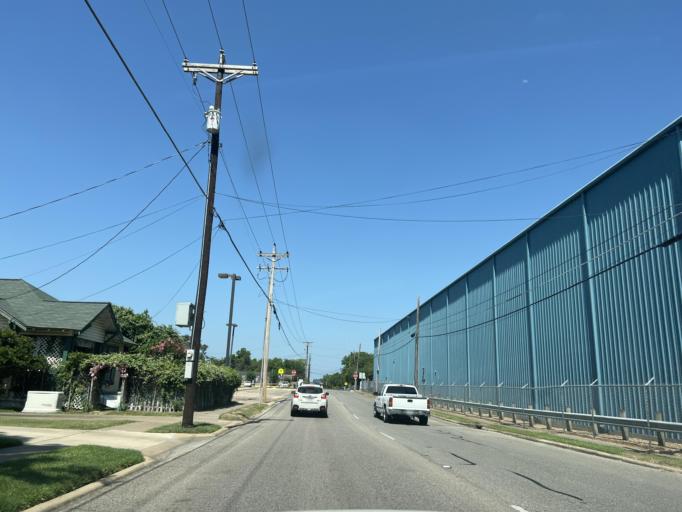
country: US
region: Texas
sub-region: Washington County
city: Brenham
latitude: 30.1681
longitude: -96.3916
